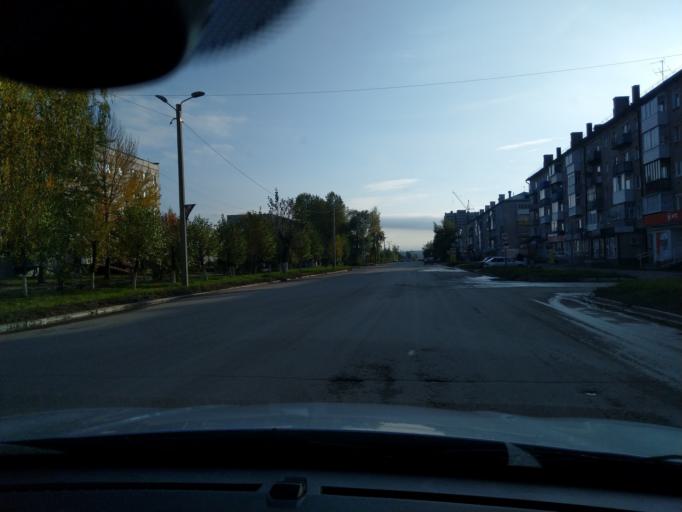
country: RU
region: Perm
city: Dobryanka
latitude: 58.4670
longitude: 56.4033
